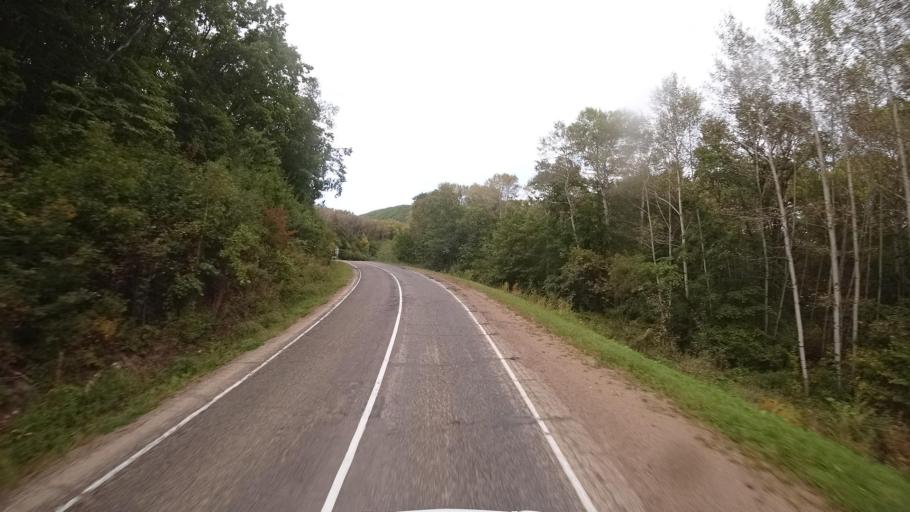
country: RU
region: Primorskiy
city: Yakovlevka
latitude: 44.3863
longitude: 133.4608
